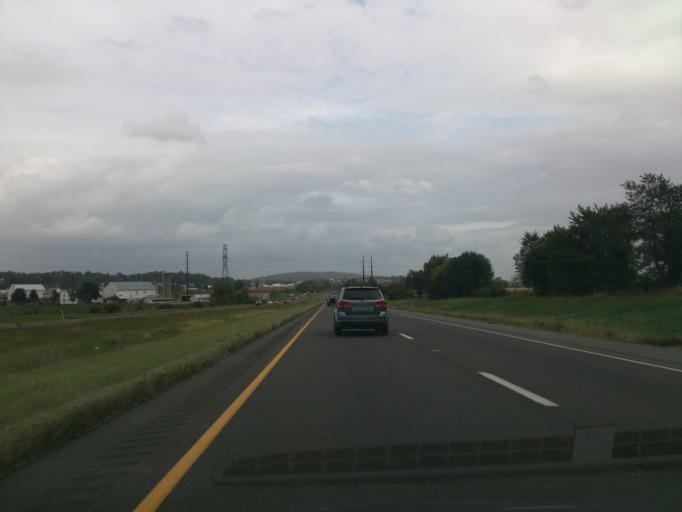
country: US
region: Pennsylvania
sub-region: Lancaster County
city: Brownstown
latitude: 40.1353
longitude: -76.2095
